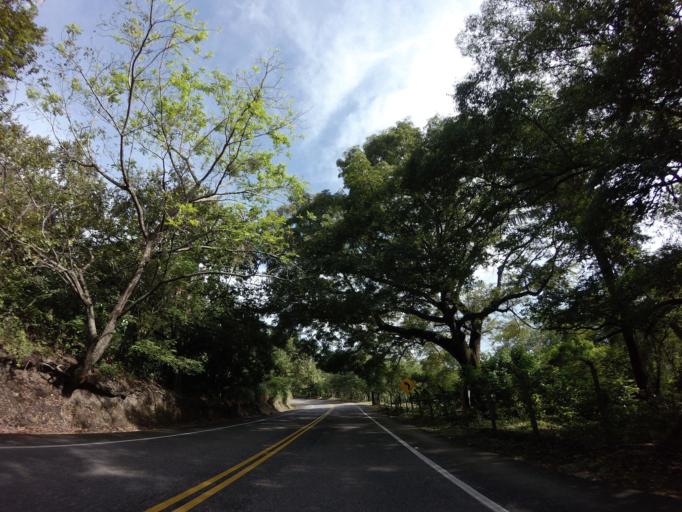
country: CO
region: Tolima
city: Honda
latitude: 5.2755
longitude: -74.7348
